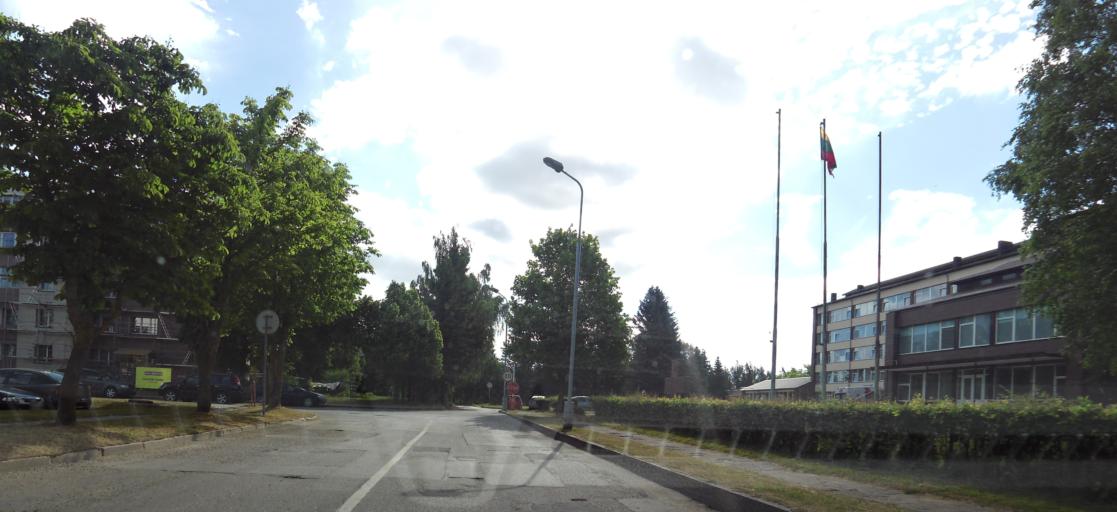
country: LT
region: Panevezys
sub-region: Birzai
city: Birzai
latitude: 56.1890
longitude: 24.7587
